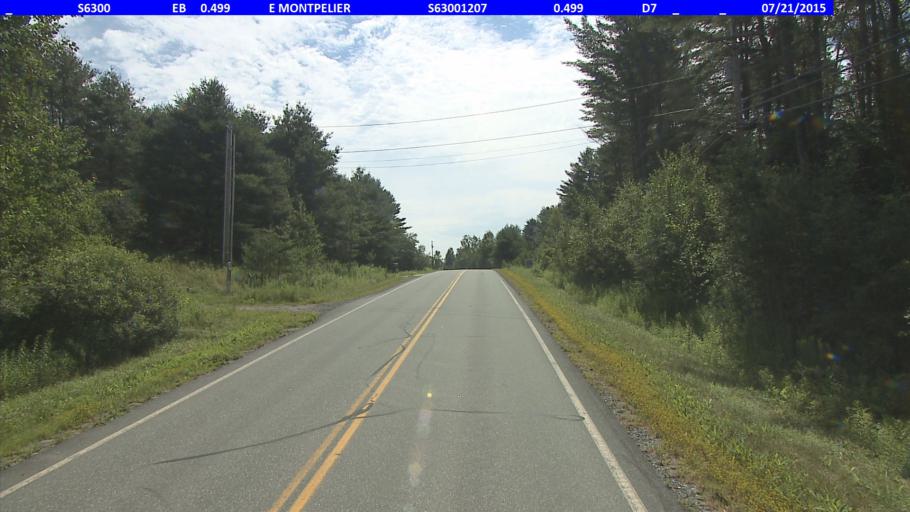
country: US
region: Vermont
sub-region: Washington County
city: Montpelier
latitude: 44.2530
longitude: -72.5310
